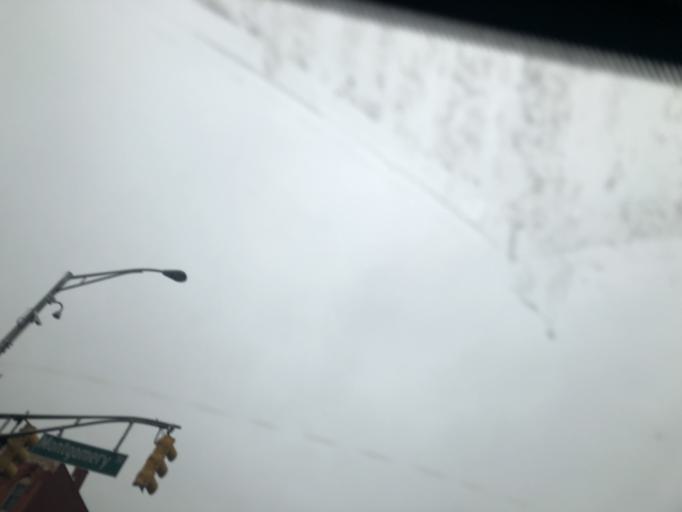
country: US
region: New Jersey
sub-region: Hudson County
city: Jersey City
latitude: 40.7256
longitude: -74.0679
